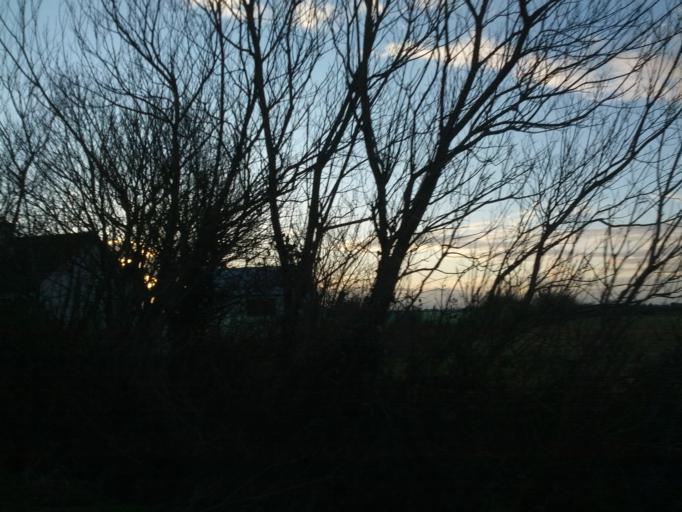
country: IE
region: Connaught
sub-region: County Galway
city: Loughrea
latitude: 53.3194
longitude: -8.6097
